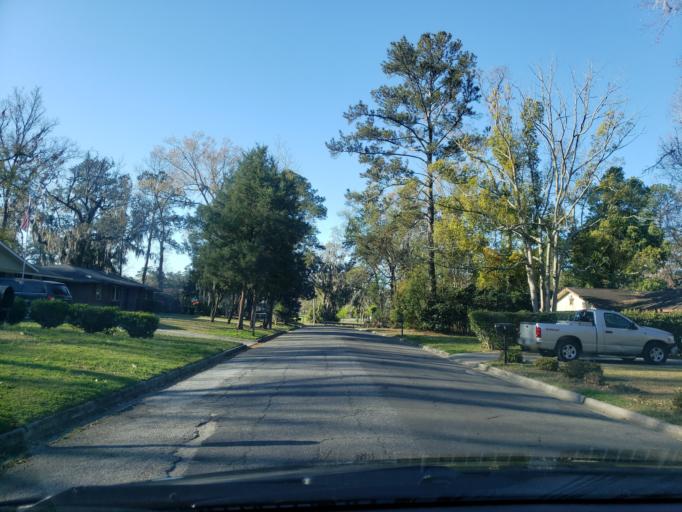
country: US
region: Georgia
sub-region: Chatham County
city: Montgomery
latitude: 31.9857
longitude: -81.1362
